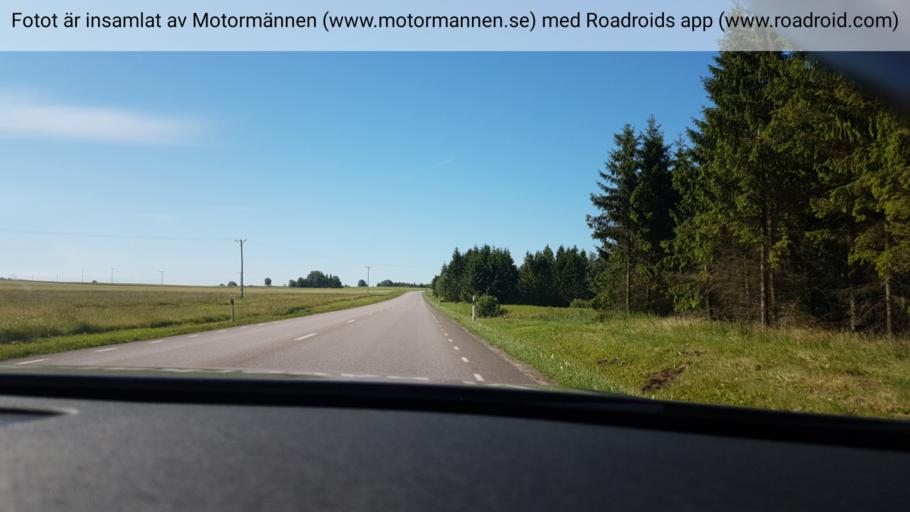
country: SE
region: Vaestra Goetaland
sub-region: Falkopings Kommun
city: Falkoeping
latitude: 58.1438
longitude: 13.5633
